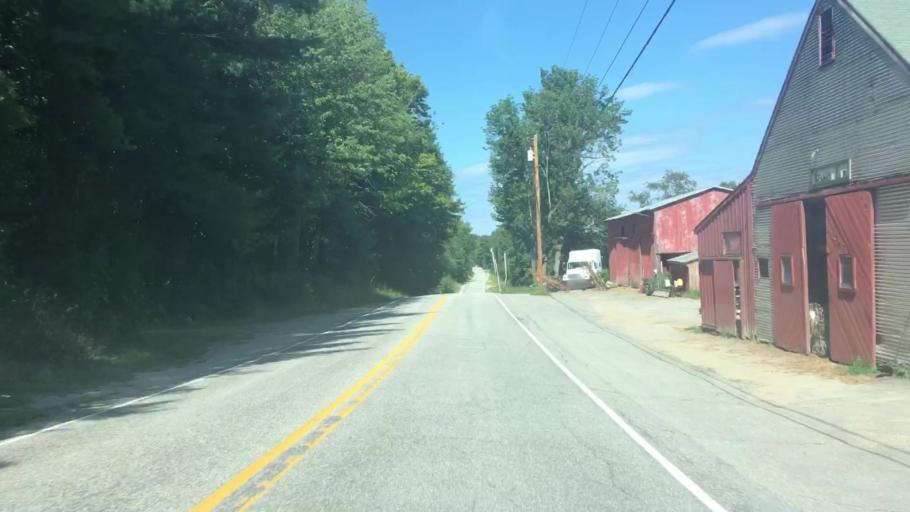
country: US
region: Maine
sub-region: Kennebec County
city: Monmouth
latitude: 44.1803
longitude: -69.9398
